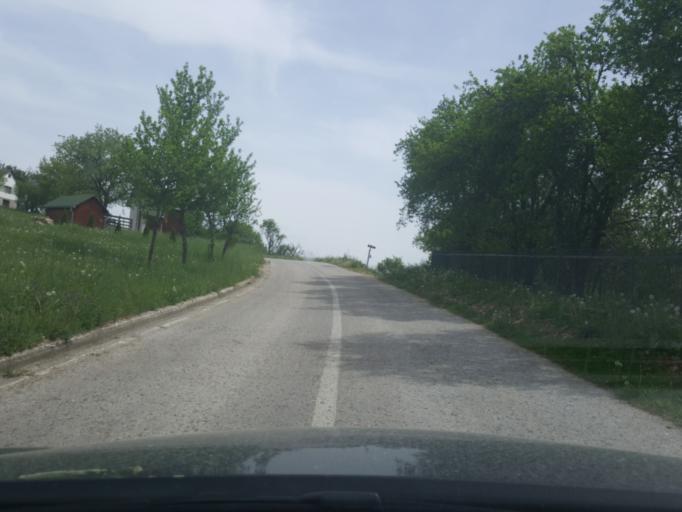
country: RS
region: Central Serbia
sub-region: Zlatiborski Okrug
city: Bajina Basta
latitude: 43.9015
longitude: 19.5109
